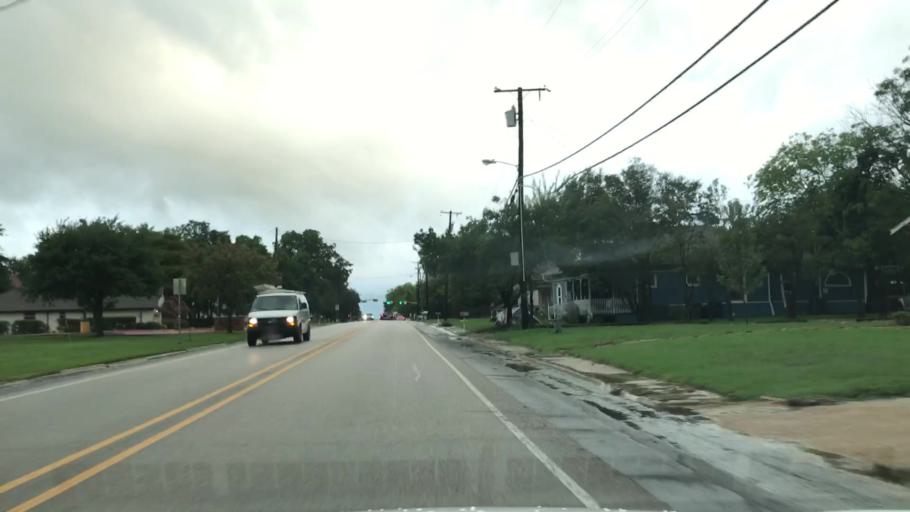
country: US
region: Texas
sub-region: Collin County
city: Wylie
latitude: 33.0195
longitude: -96.5388
